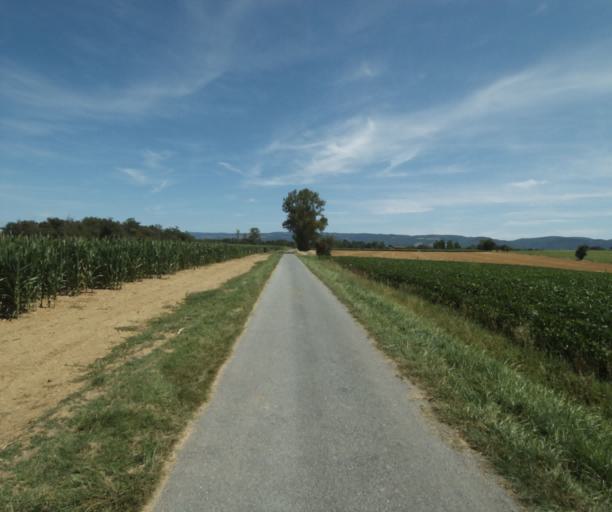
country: FR
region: Midi-Pyrenees
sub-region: Departement de la Haute-Garonne
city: Revel
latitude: 43.5095
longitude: 2.0157
